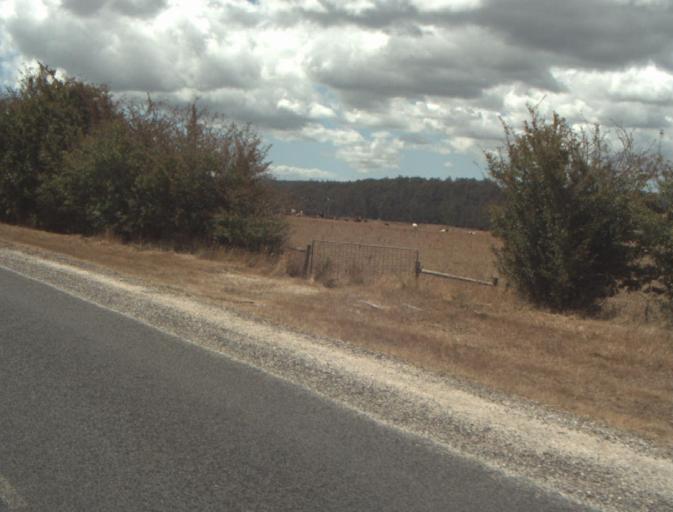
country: AU
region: Tasmania
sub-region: Launceston
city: Mayfield
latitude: -41.2315
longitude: 147.1248
